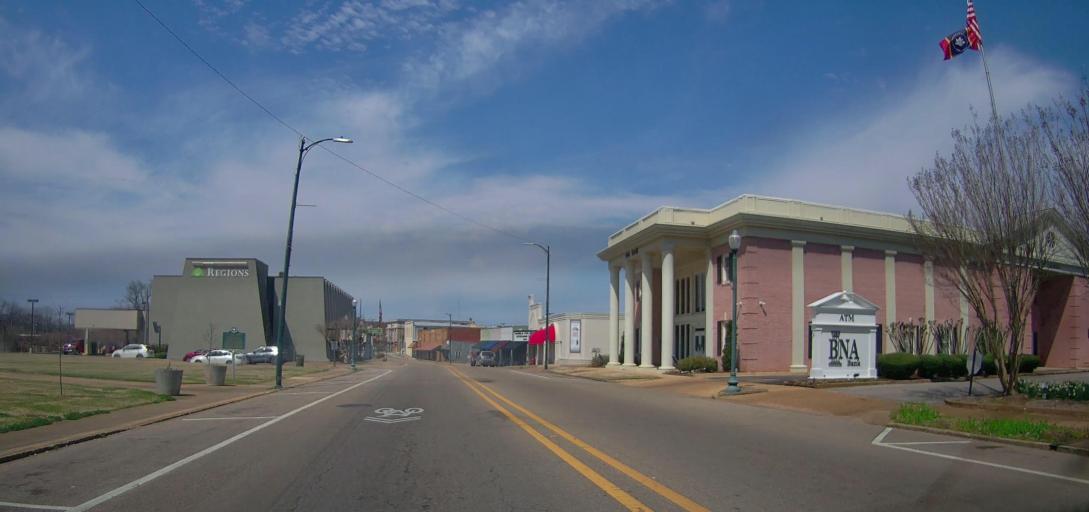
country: US
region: Mississippi
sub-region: Union County
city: New Albany
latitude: 34.4928
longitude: -89.0069
